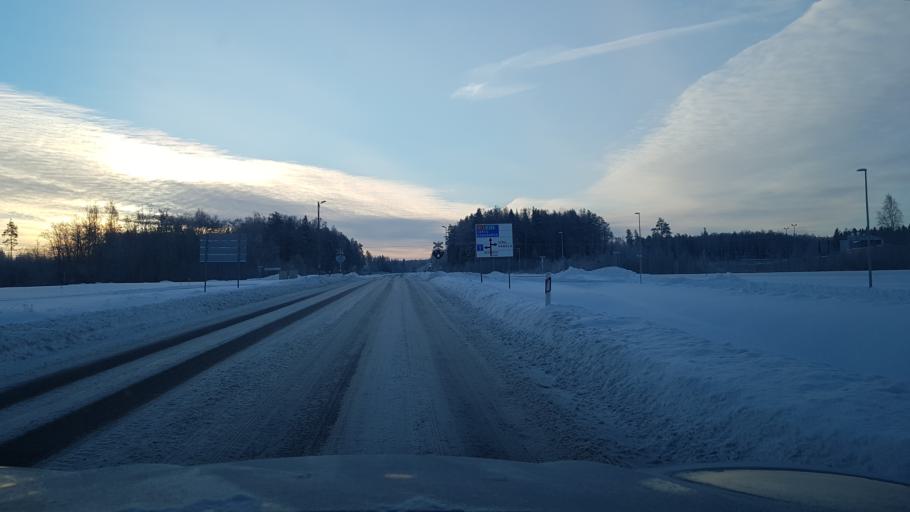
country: EE
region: Ida-Virumaa
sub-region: Johvi vald
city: Johvi
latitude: 59.3612
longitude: 27.4616
